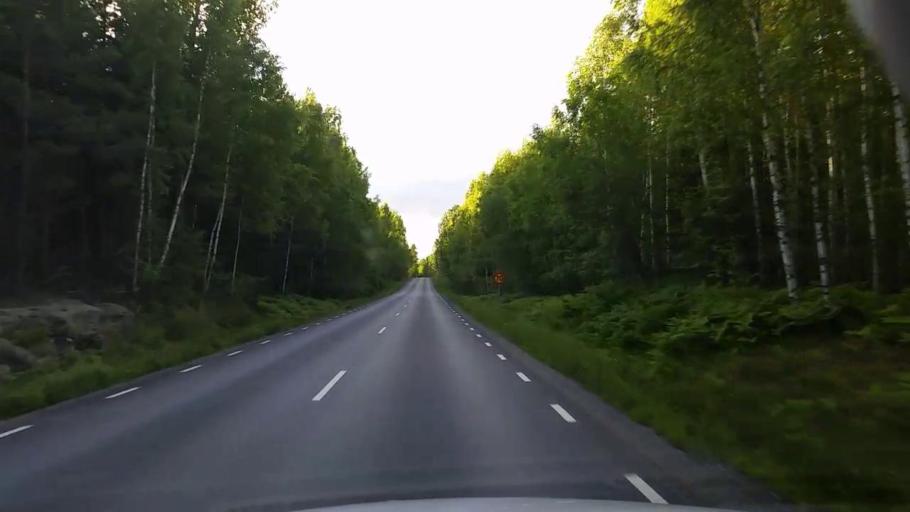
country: SE
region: Vaestmanland
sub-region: Kopings Kommun
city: Kolsva
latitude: 59.6866
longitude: 15.8375
